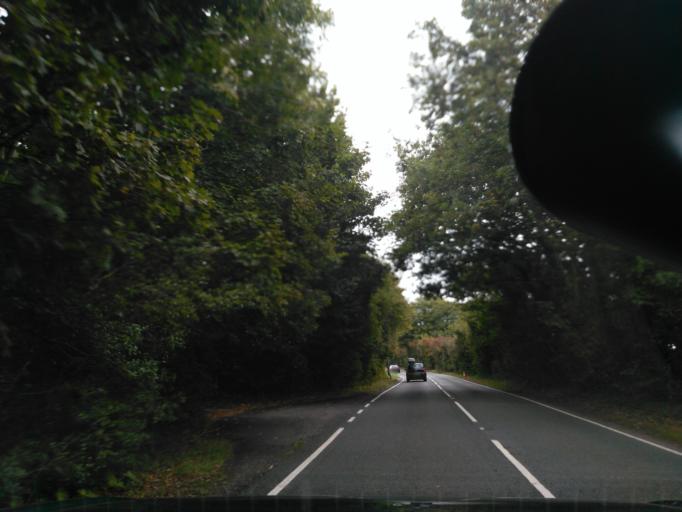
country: GB
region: England
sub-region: Dorset
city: Lytchett Matravers
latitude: 50.7396
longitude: -2.1062
